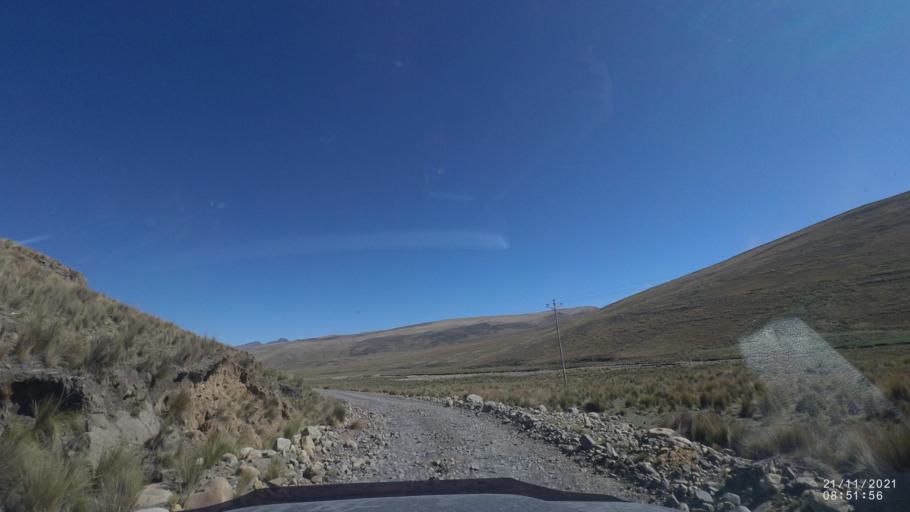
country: BO
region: Cochabamba
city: Cochabamba
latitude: -17.2161
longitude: -66.2378
